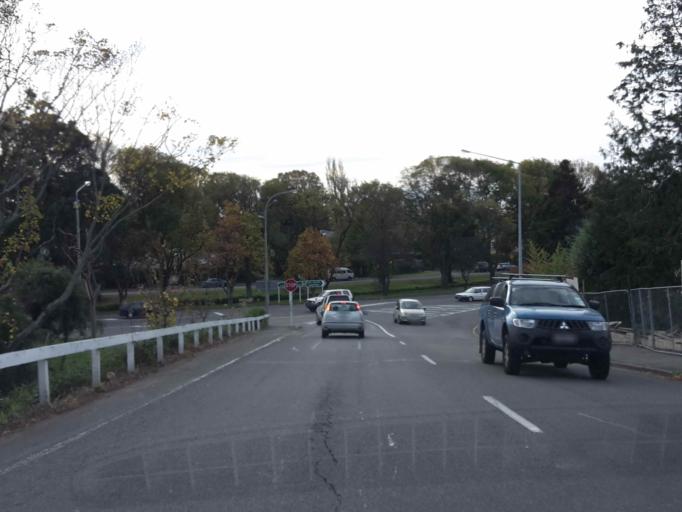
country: NZ
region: Canterbury
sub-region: Christchurch City
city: Christchurch
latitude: -43.5698
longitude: 172.6237
